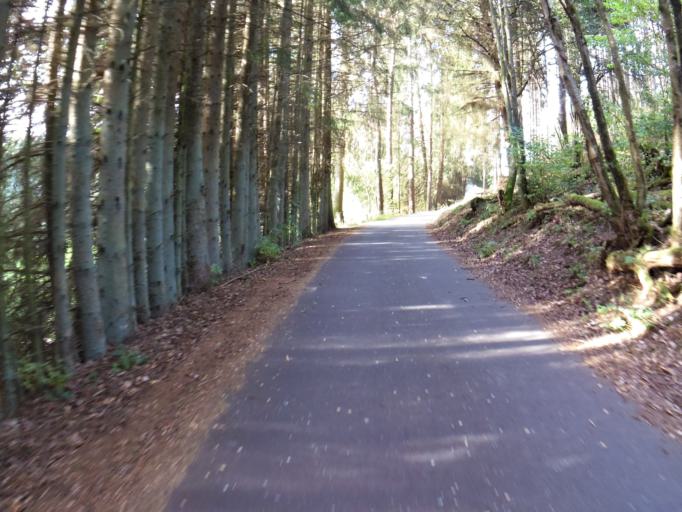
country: BE
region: Wallonia
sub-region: Province de Liege
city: Saint-Vith
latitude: 50.2477
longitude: 6.1472
